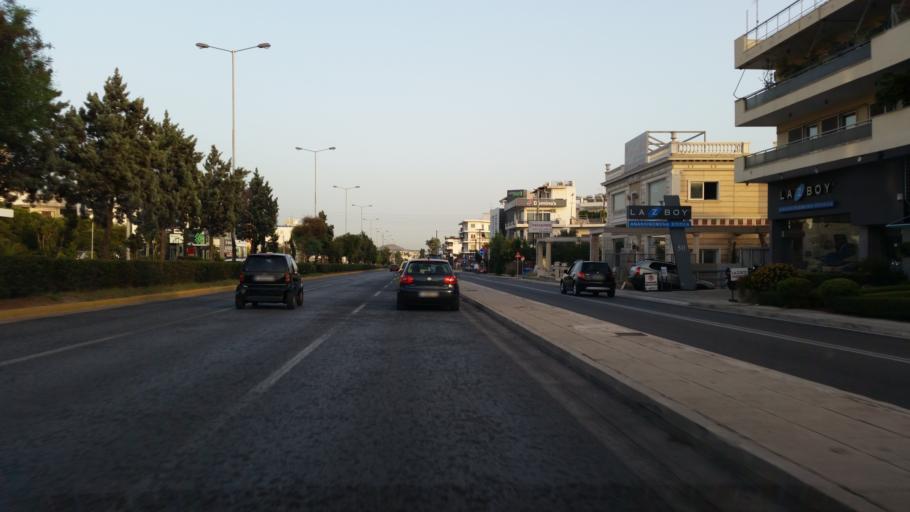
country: GR
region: Attica
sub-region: Nomarchia Athinas
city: Glyfada
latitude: 37.8803
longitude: 23.7539
